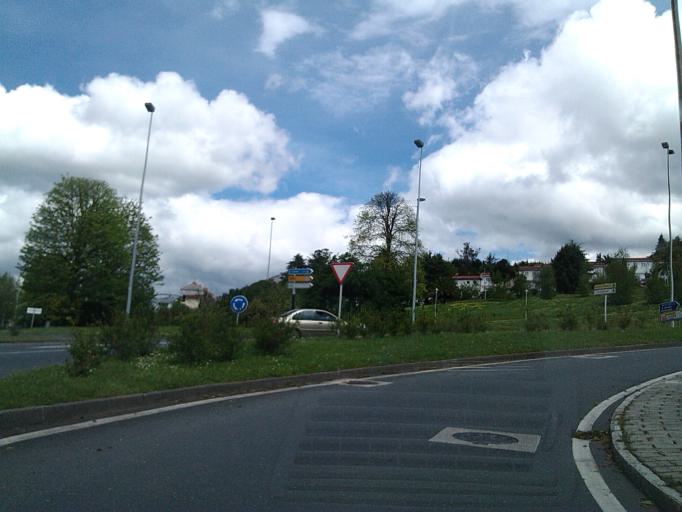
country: ES
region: Galicia
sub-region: Provincia da Coruna
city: Santiago de Compostela
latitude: 42.8890
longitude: -8.5322
